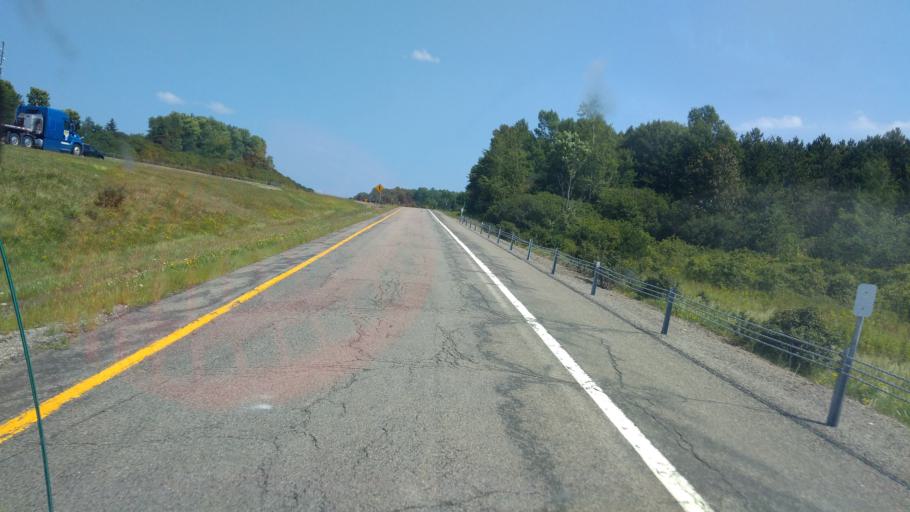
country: US
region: New York
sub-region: Allegany County
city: Alfred
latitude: 42.3052
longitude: -77.8744
